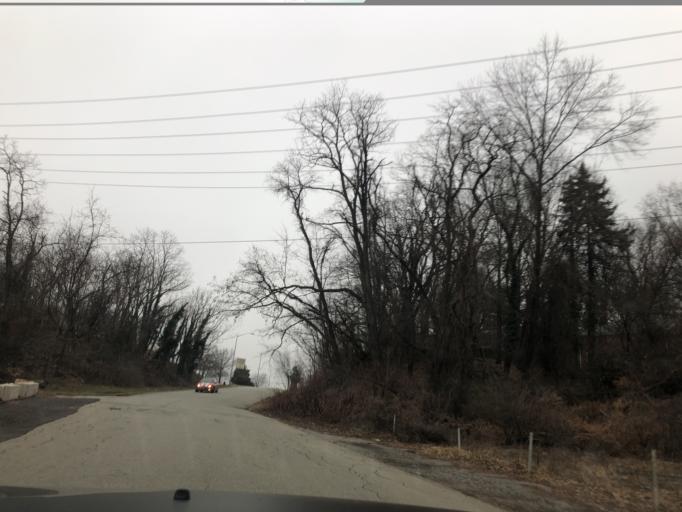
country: US
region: Pennsylvania
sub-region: Allegheny County
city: Churchill
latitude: 40.4557
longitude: -79.8600
